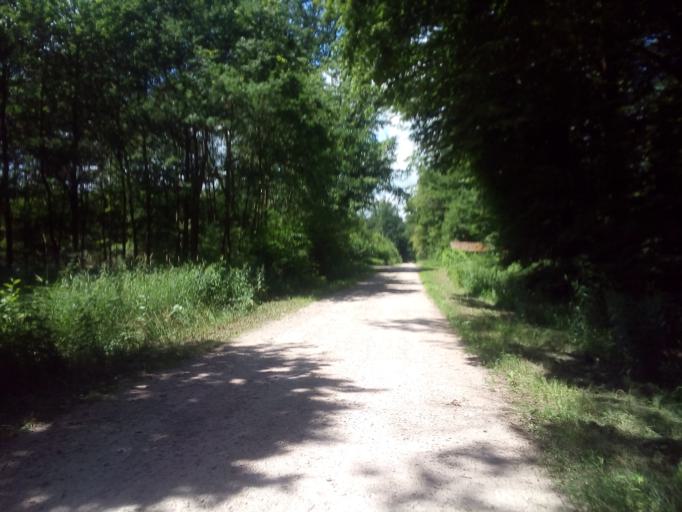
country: DE
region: Baden-Wuerttemberg
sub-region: Freiburg Region
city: Rheinau
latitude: 48.6384
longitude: 7.9659
